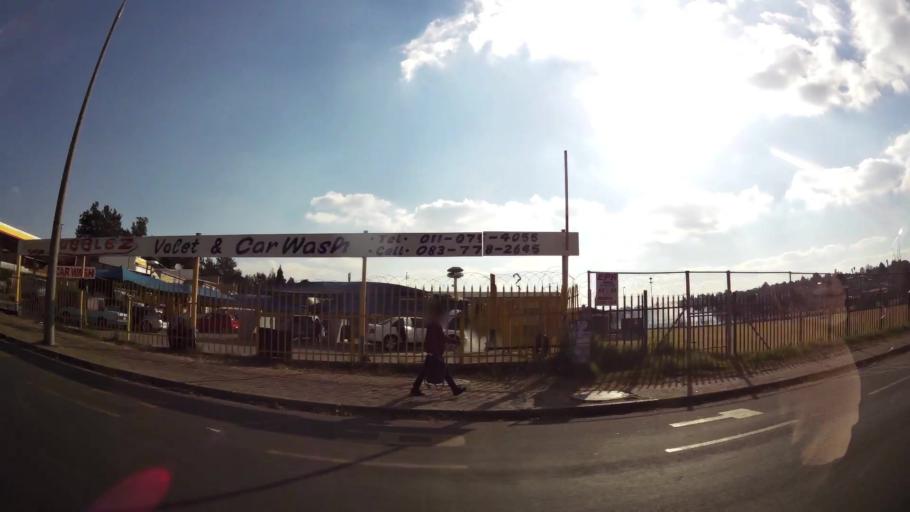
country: ZA
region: Gauteng
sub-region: West Rand District Municipality
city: Krugersdorp
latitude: -26.0977
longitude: 27.7749
